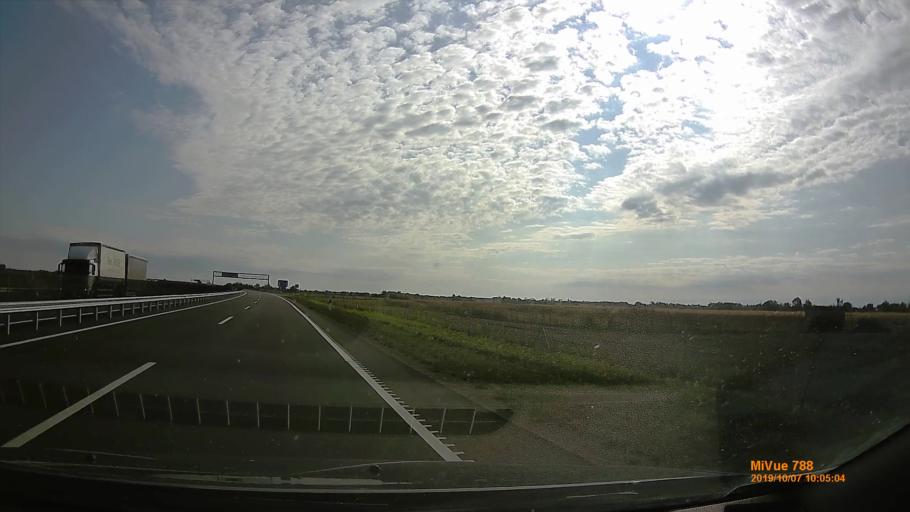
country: HU
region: Bekes
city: Kondoros
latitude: 46.7379
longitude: 20.7906
